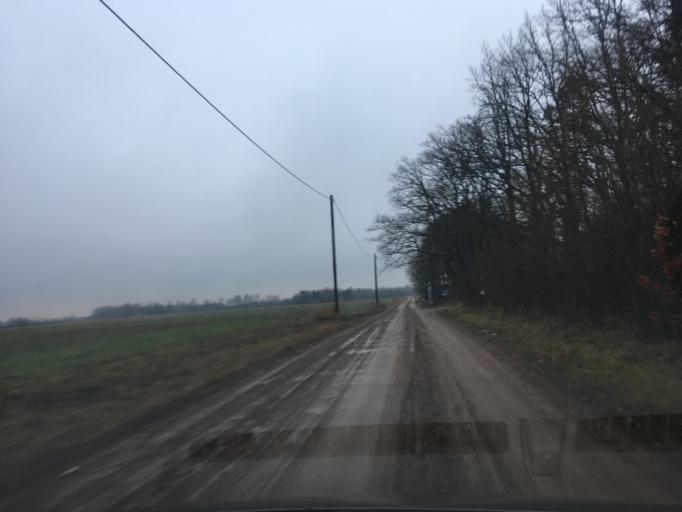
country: EE
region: Tartu
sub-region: Tartu linn
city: Tartu
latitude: 58.3839
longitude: 26.9271
